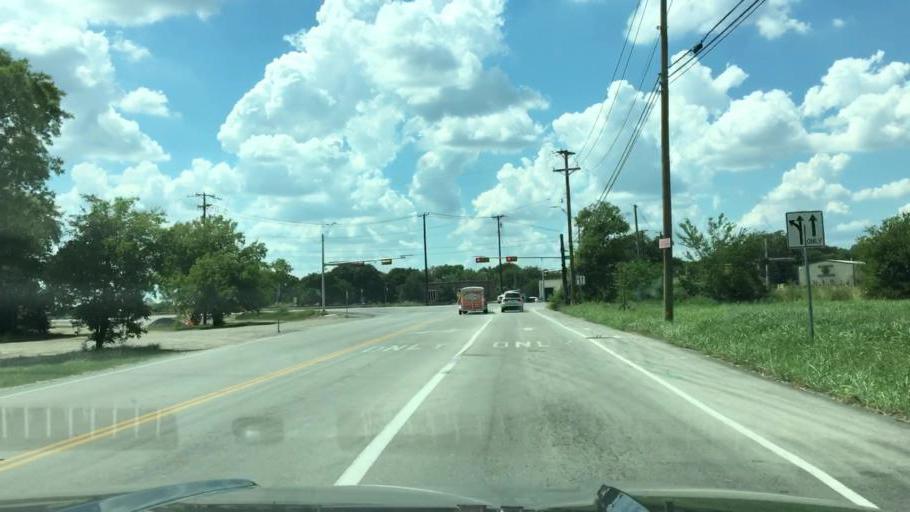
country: US
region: Texas
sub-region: Tarrant County
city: Haslet
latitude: 32.9746
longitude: -97.3462
